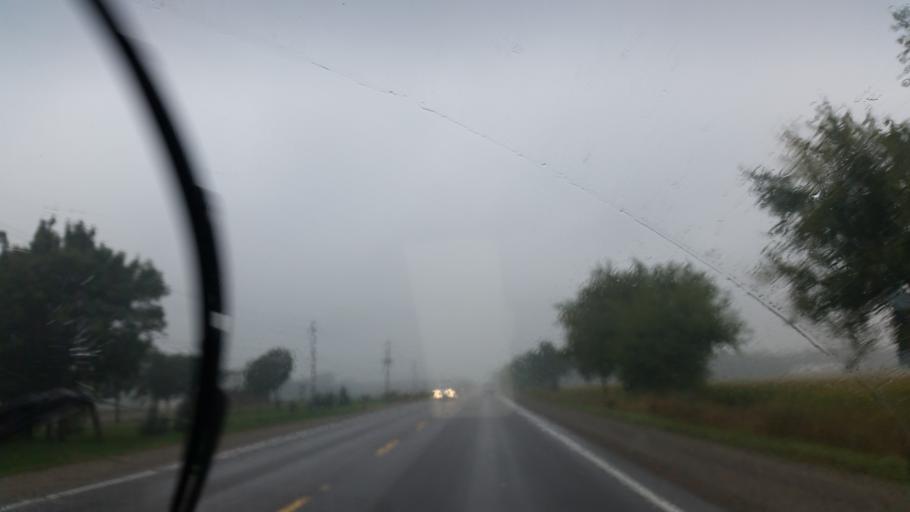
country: CA
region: Ontario
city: Stratford
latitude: 43.2818
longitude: -81.0581
